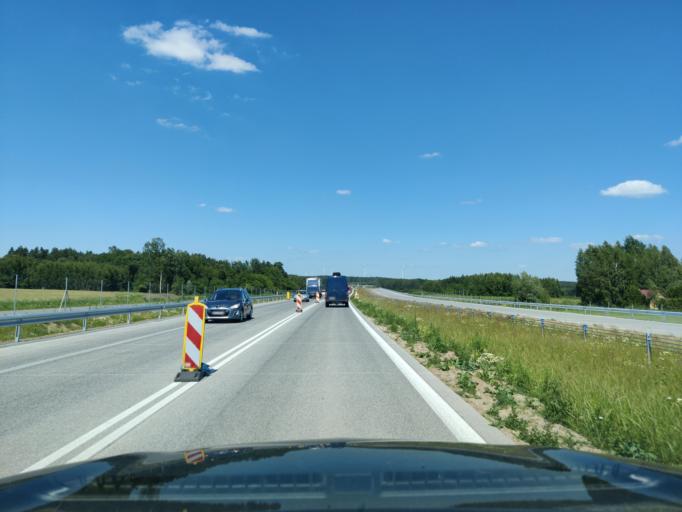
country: PL
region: Masovian Voivodeship
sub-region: Powiat mlawski
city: Mlawa
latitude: 53.1276
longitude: 20.4141
